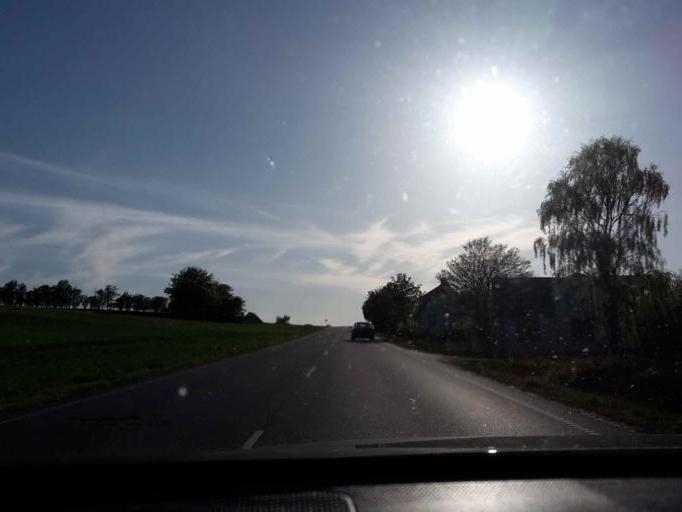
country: DK
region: Central Jutland
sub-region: Norddjurs Kommune
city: Allingabro
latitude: 56.4466
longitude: 10.2741
